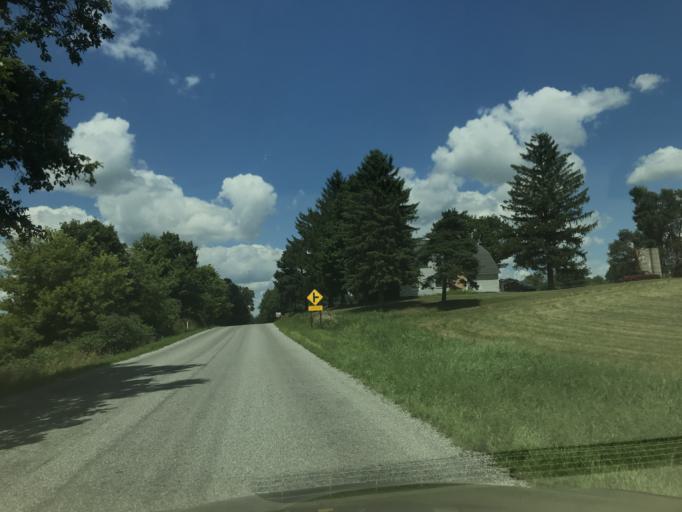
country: US
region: Michigan
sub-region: Ingham County
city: Holt
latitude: 42.6128
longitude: -84.5625
